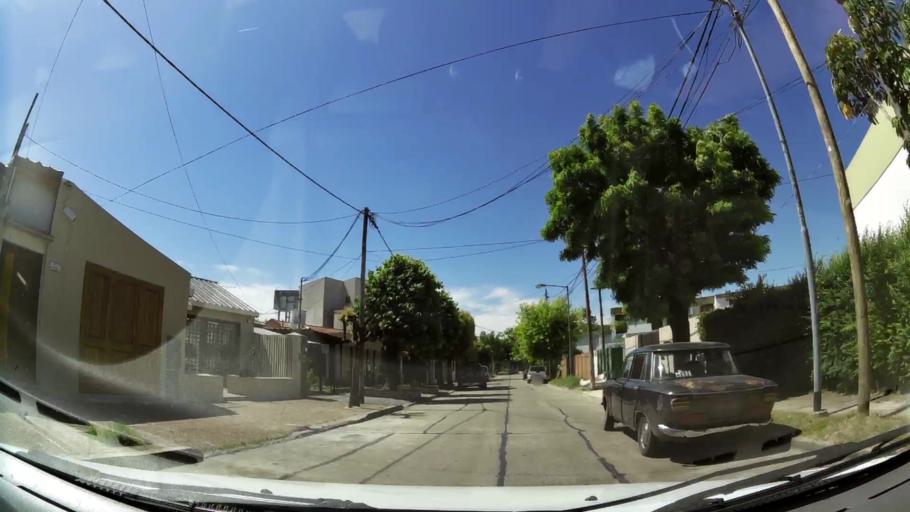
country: AR
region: Buenos Aires
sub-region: Partido de General San Martin
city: General San Martin
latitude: -34.5610
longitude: -58.5528
